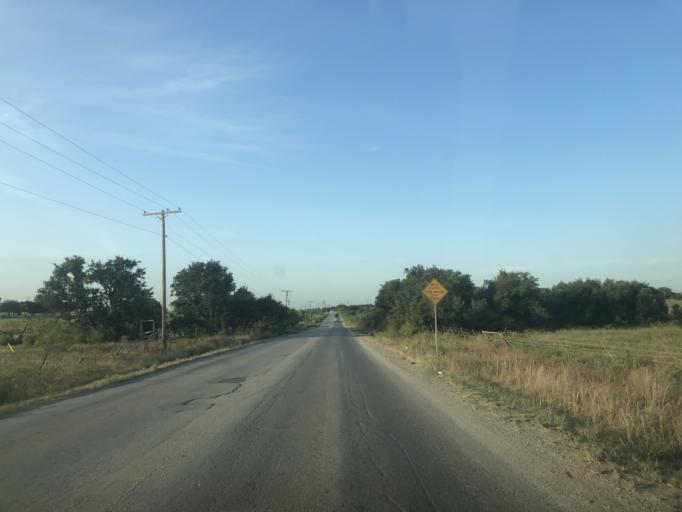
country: US
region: Texas
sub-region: Tarrant County
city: White Settlement
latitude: 32.7826
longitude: -97.4868
